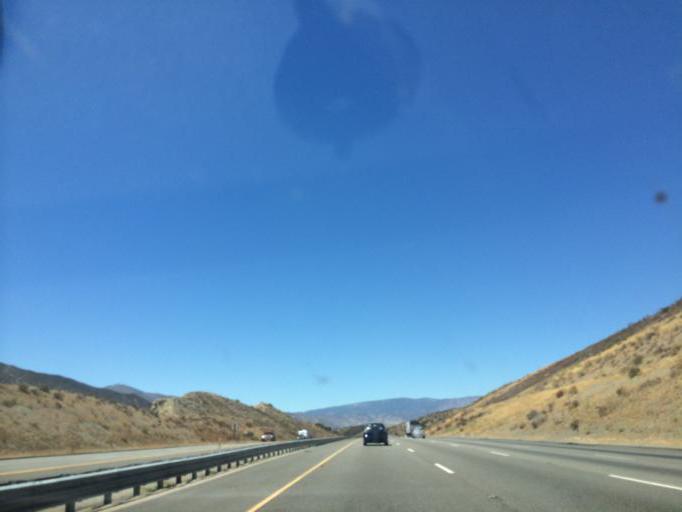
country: US
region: California
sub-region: Los Angeles County
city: Castaic
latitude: 34.6366
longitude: -118.7422
